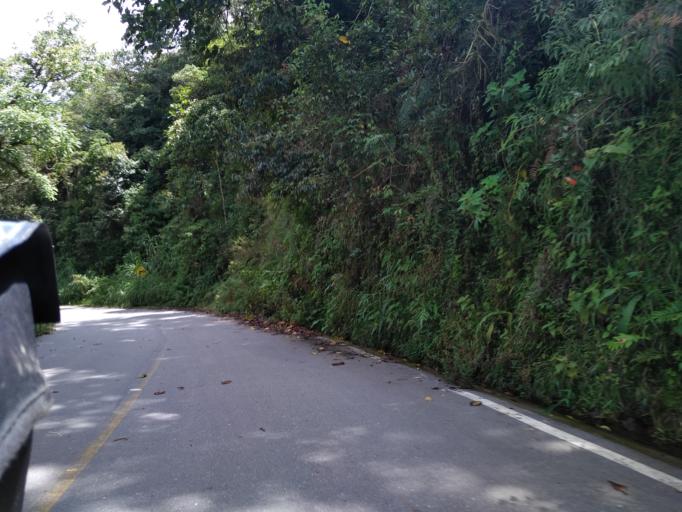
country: CO
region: Santander
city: Oiba
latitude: 6.1883
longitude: -73.1819
